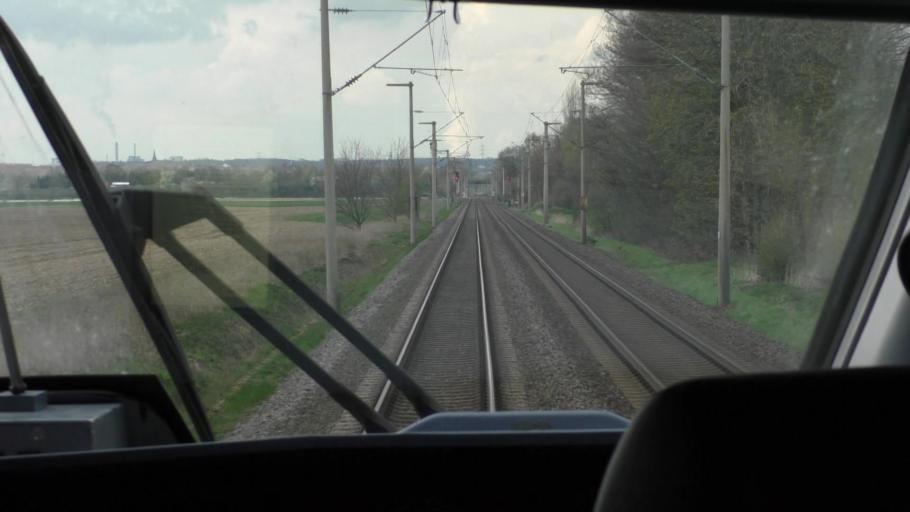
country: DE
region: North Rhine-Westphalia
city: Wesseling
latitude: 50.8069
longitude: 6.9413
